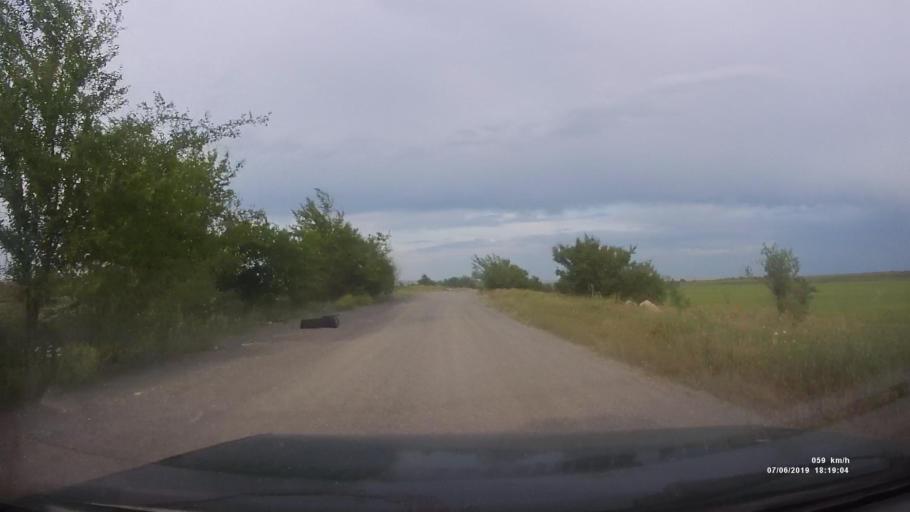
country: RU
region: Rostov
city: Staraya Stanitsa
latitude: 48.2559
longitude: 40.3684
